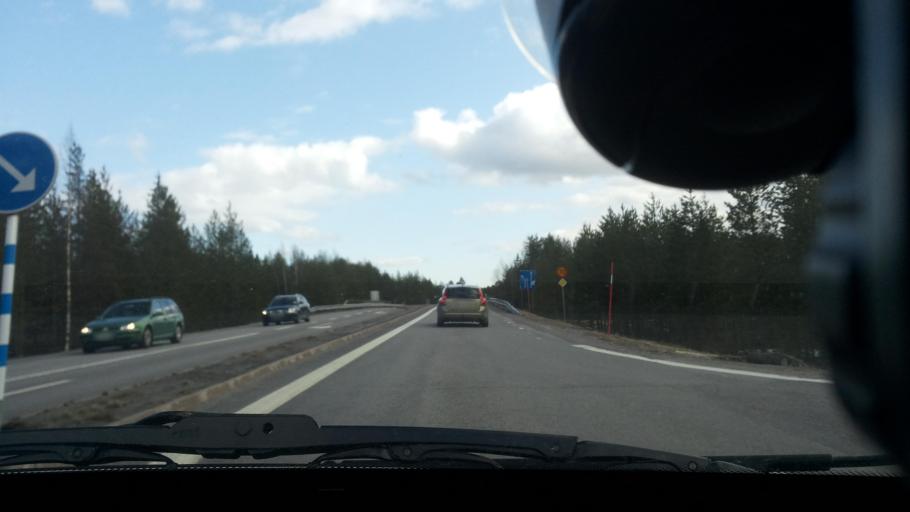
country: SE
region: Norrbotten
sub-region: Lulea Kommun
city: Gammelstad
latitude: 65.5989
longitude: 22.0416
